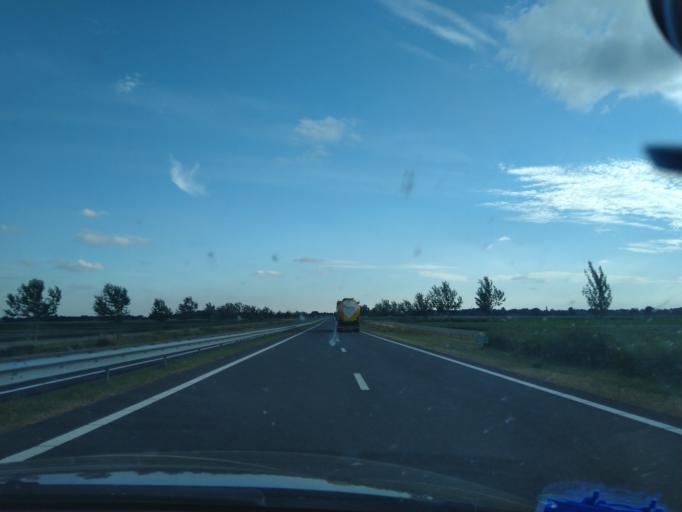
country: NL
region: Groningen
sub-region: Gemeente Veendam
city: Veendam
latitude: 53.0614
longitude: 6.8698
